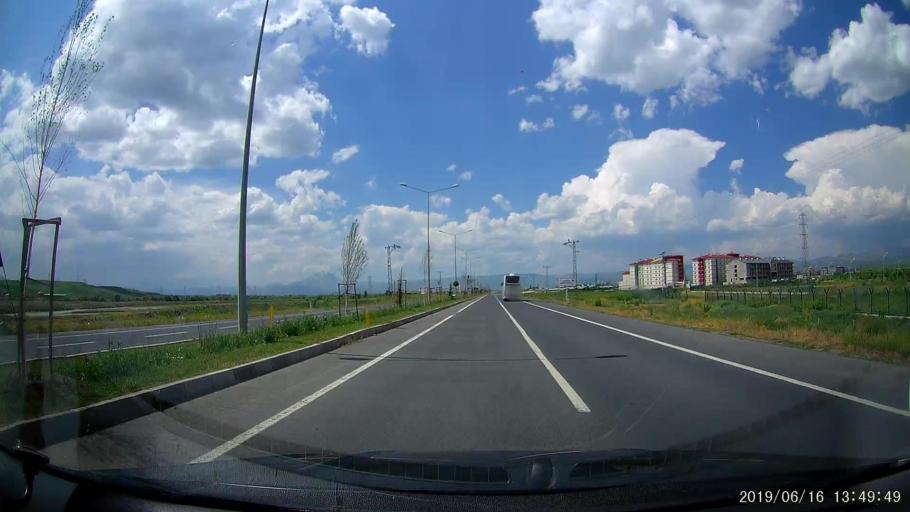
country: TR
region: Agri
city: Agri
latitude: 39.7206
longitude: 42.9862
